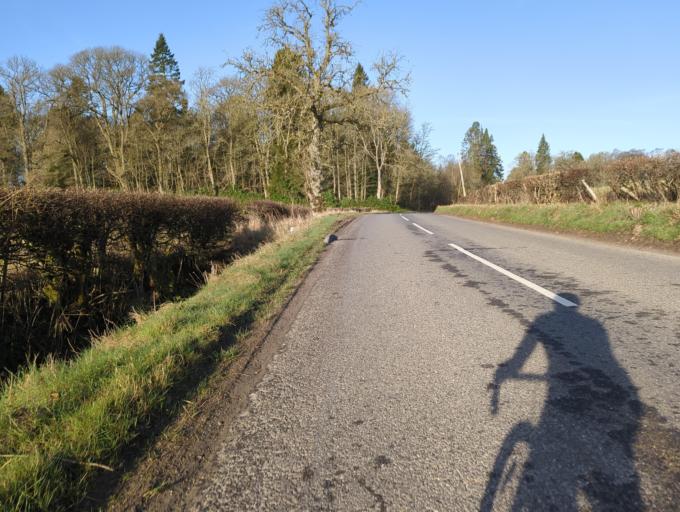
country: GB
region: Scotland
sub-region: Perth and Kinross
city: Methven
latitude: 56.4539
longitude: -3.5404
